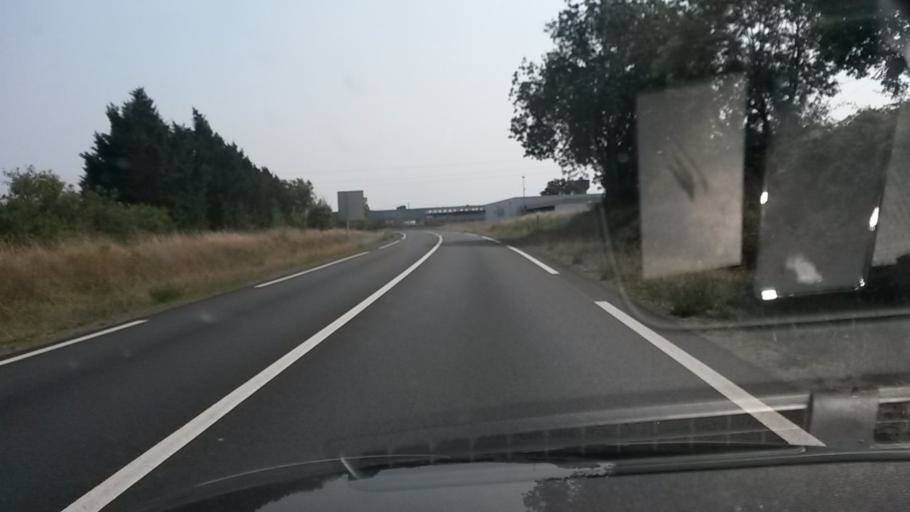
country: FR
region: Pays de la Loire
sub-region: Departement de la Loire-Atlantique
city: Ancenis
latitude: 47.3813
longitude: -1.1730
